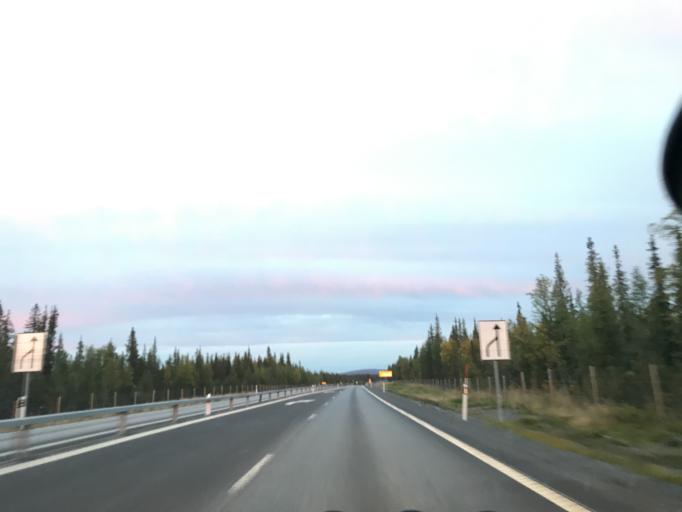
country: SE
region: Norrbotten
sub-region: Gallivare Kommun
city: Malmberget
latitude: 67.6894
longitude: 20.8404
